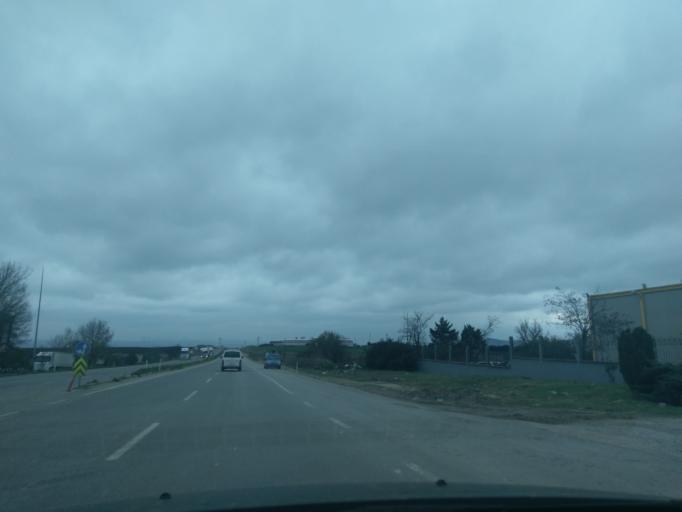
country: TR
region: Istanbul
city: Muratbey
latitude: 41.1157
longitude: 28.4980
